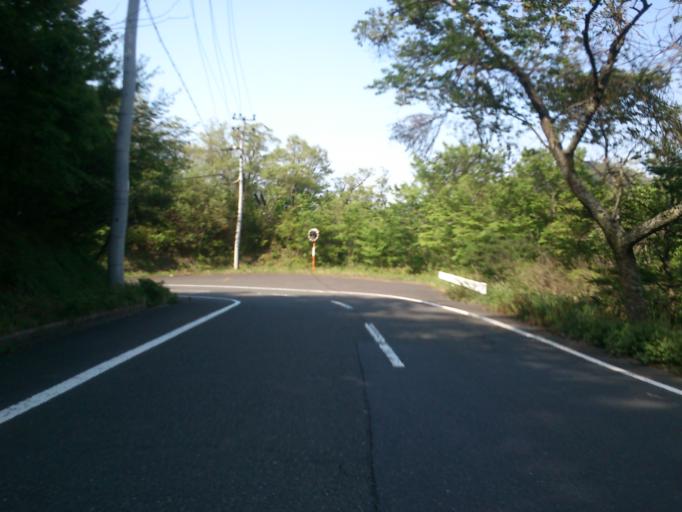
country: JP
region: Kyoto
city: Miyazu
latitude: 35.7253
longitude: 135.1879
